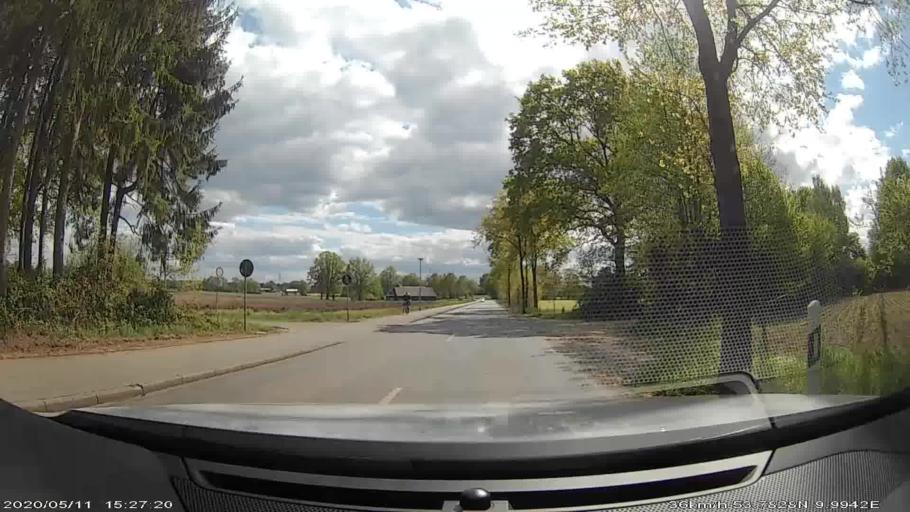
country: DE
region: Schleswig-Holstein
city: Henstedt-Ulzburg
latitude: 53.7702
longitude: 9.9934
